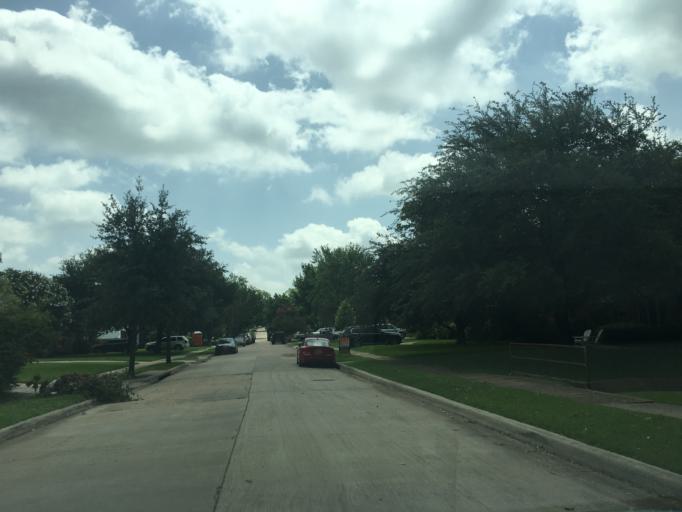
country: US
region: Texas
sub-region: Dallas County
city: University Park
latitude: 32.8715
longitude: -96.7947
